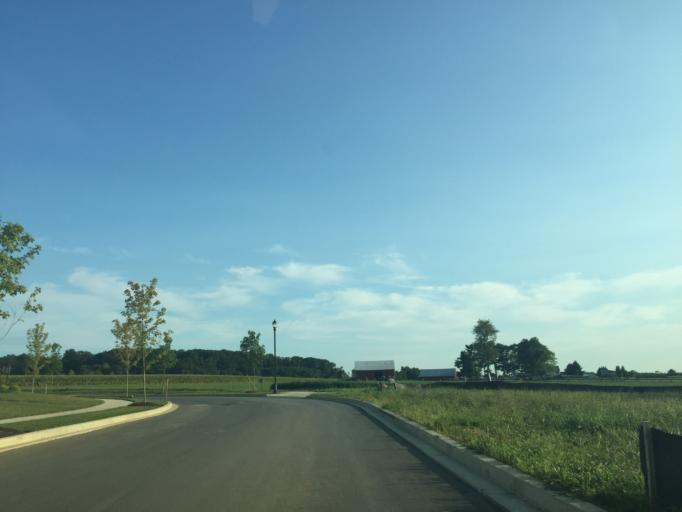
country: US
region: Maryland
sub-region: Frederick County
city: Green Valley
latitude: 39.3524
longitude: -77.2870
